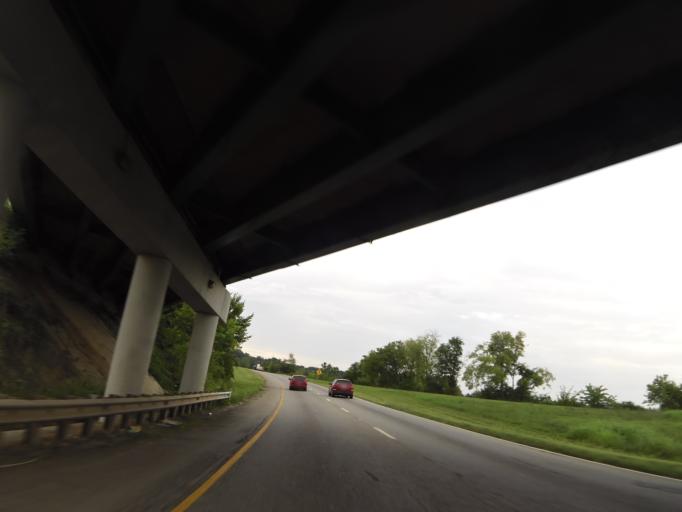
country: US
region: Tennessee
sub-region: Blount County
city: Alcoa
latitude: 35.7882
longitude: -83.9916
